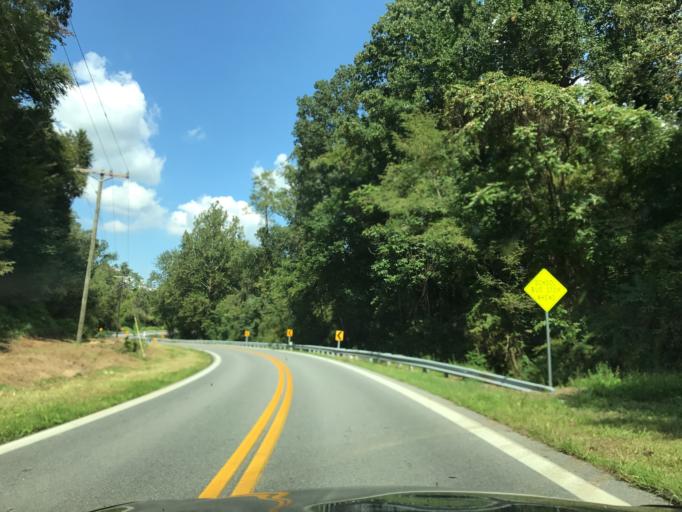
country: US
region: Delaware
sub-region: New Castle County
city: Townsend
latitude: 39.3705
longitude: -75.8039
